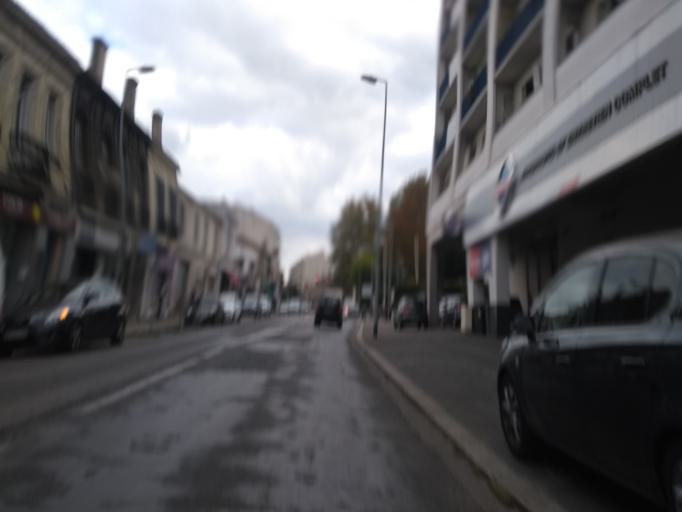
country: FR
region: Aquitaine
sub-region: Departement de la Gironde
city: Talence
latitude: 44.8134
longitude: -0.5732
